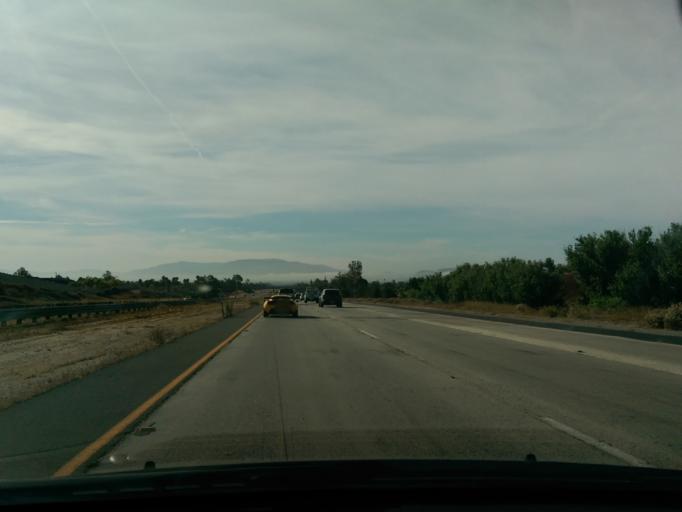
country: US
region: California
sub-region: Riverside County
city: Murrieta
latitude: 33.5838
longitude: -117.2313
